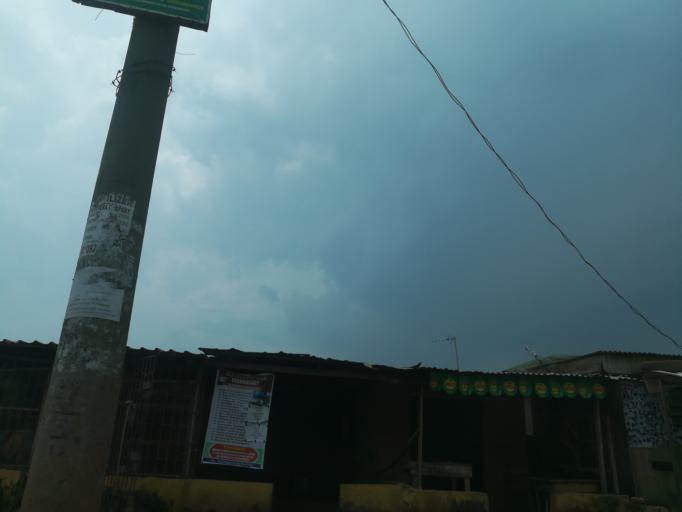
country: NG
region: Lagos
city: Ikorodu
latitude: 6.5736
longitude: 3.5921
